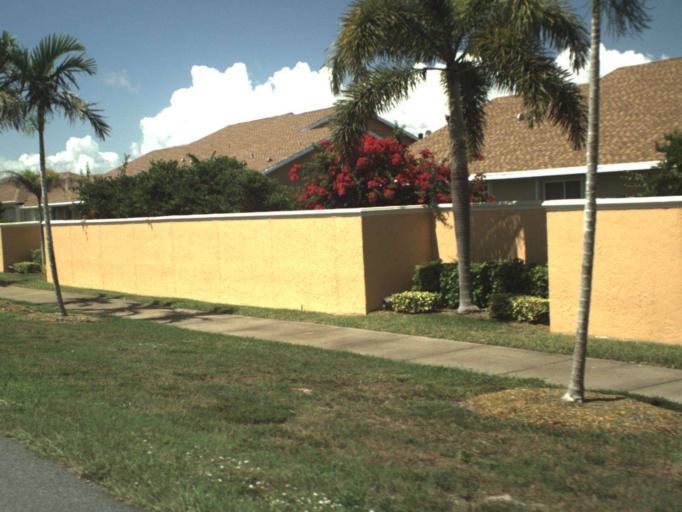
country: US
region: Florida
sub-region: Saint Lucie County
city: Fort Pierce
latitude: 27.4915
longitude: -80.2998
